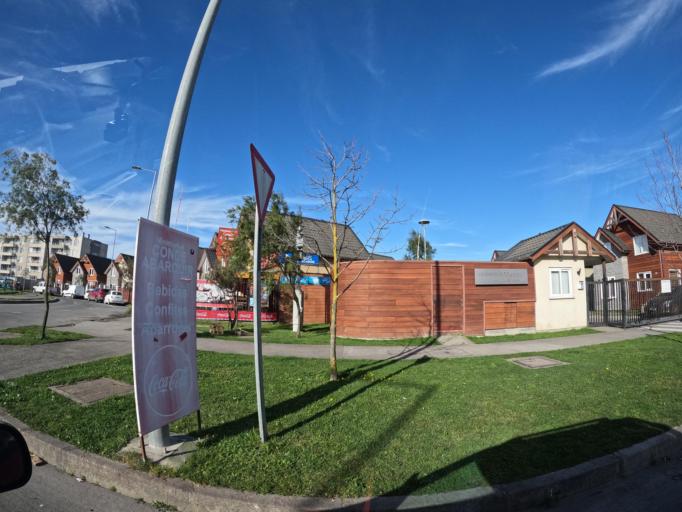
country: CL
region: Biobio
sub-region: Provincia de Concepcion
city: Concepcion
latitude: -36.7691
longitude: -73.0702
